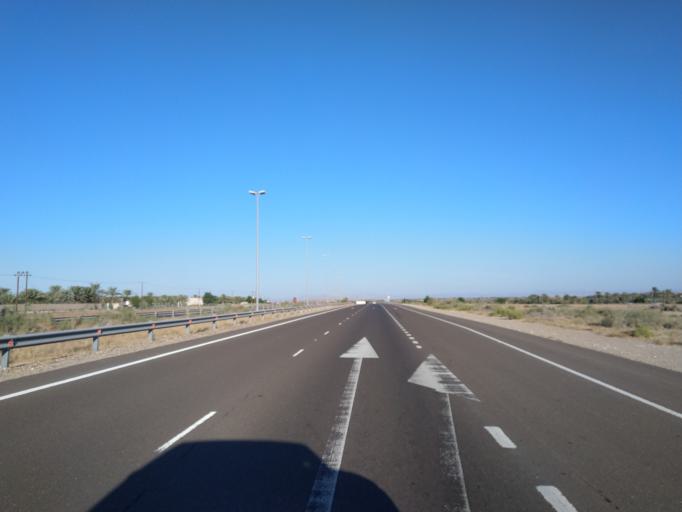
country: OM
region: Al Buraimi
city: Al Buraymi
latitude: 24.5412
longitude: 55.6371
